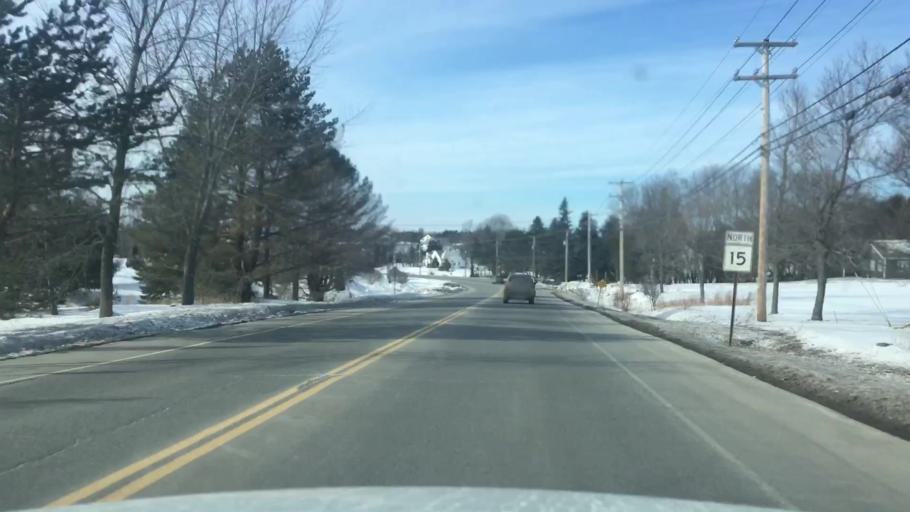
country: US
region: Maine
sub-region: Penobscot County
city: Bangor
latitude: 44.8501
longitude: -68.8047
